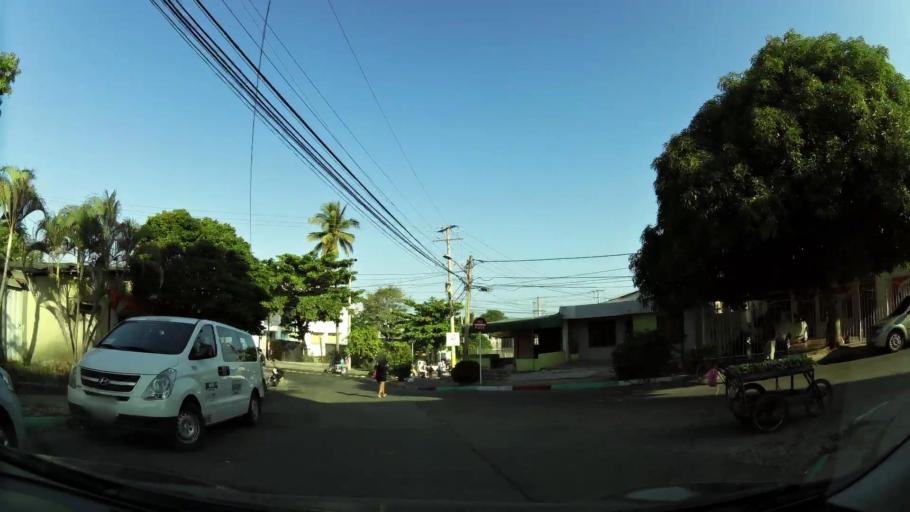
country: CO
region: Bolivar
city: Cartagena
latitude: 10.4056
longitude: -75.5020
